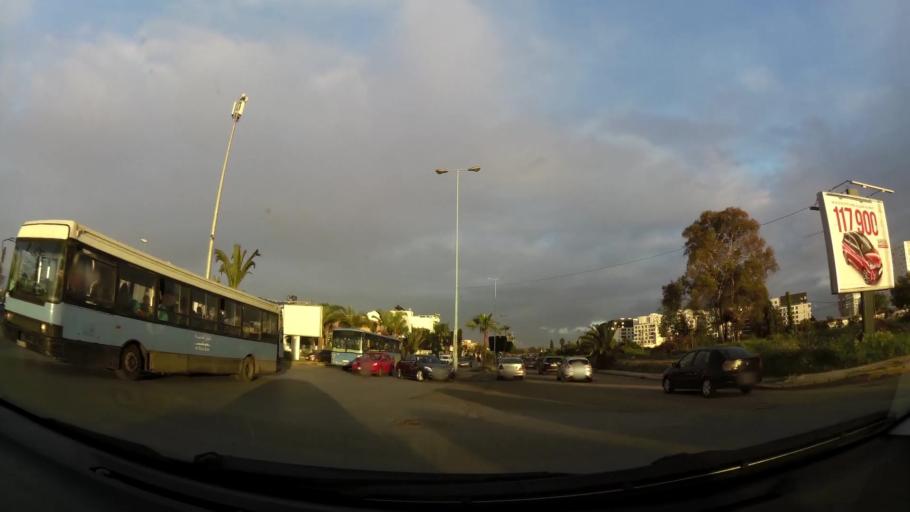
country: MA
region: Grand Casablanca
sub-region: Casablanca
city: Casablanca
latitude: 33.5697
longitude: -7.6623
